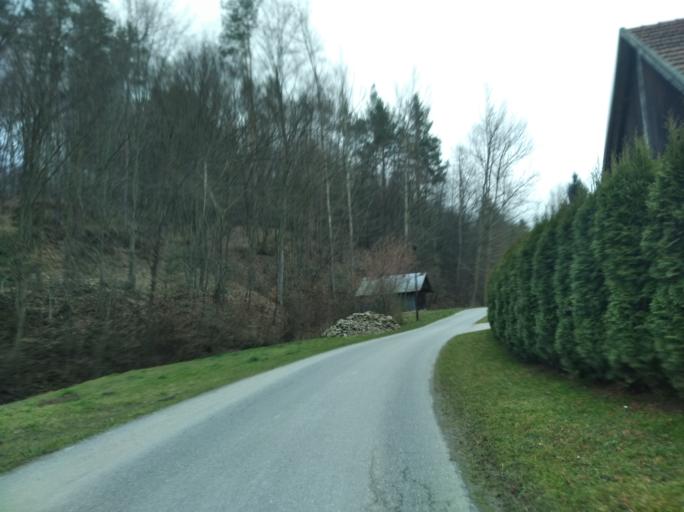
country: PL
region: Subcarpathian Voivodeship
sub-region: Powiat strzyzowski
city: Strzyzow
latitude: 49.8605
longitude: 21.8321
